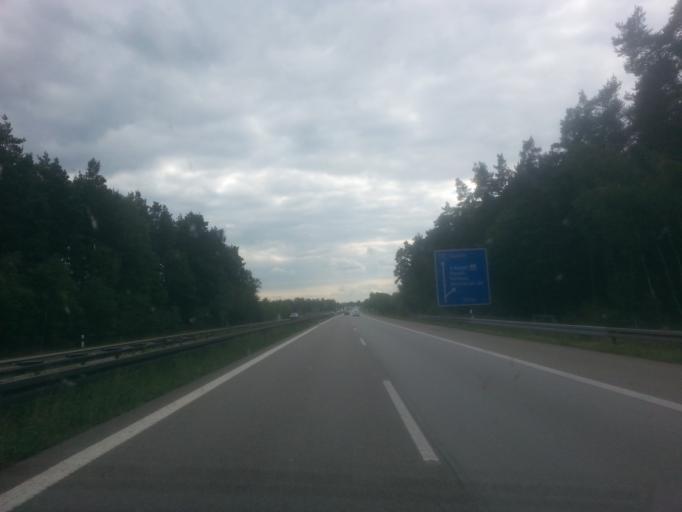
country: DE
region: Bavaria
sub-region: Upper Palatinate
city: Steinberg
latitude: 49.2839
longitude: 12.1381
